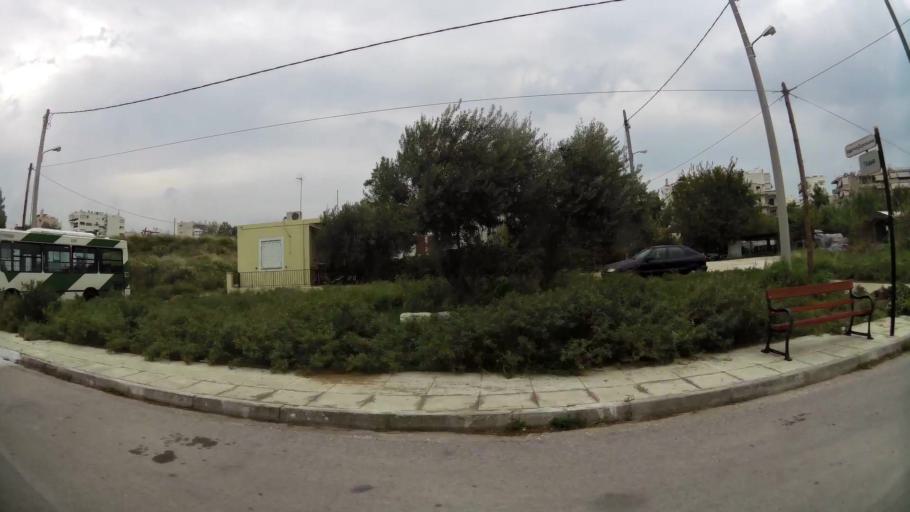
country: GR
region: Attica
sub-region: Nomarchia Athinas
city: Palaio Faliro
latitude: 37.9255
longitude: 23.7168
